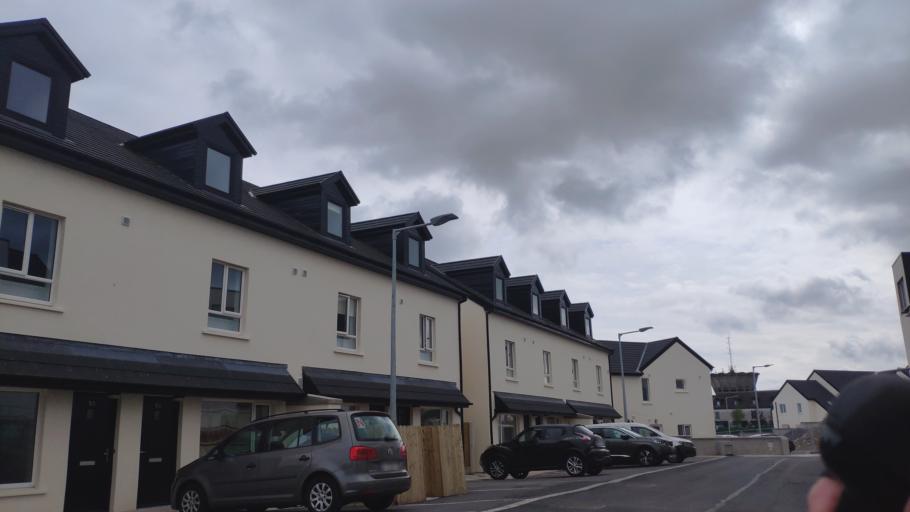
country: IE
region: Munster
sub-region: County Cork
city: Cork
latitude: 51.9120
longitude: -8.5019
